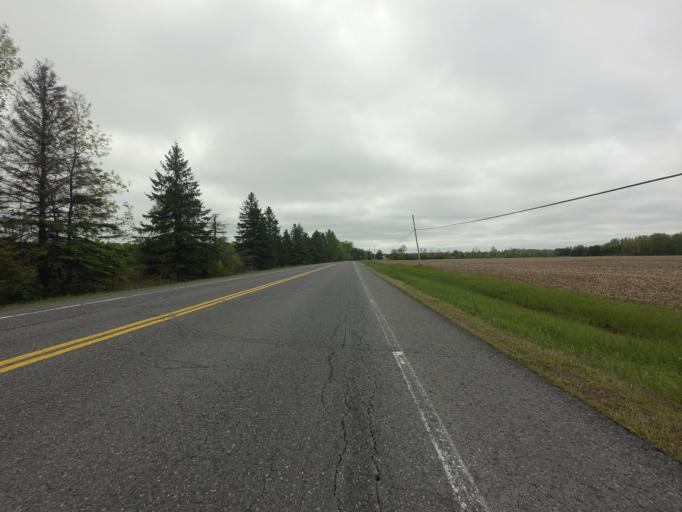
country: CA
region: Ontario
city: Casselman
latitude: 45.0550
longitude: -75.2014
